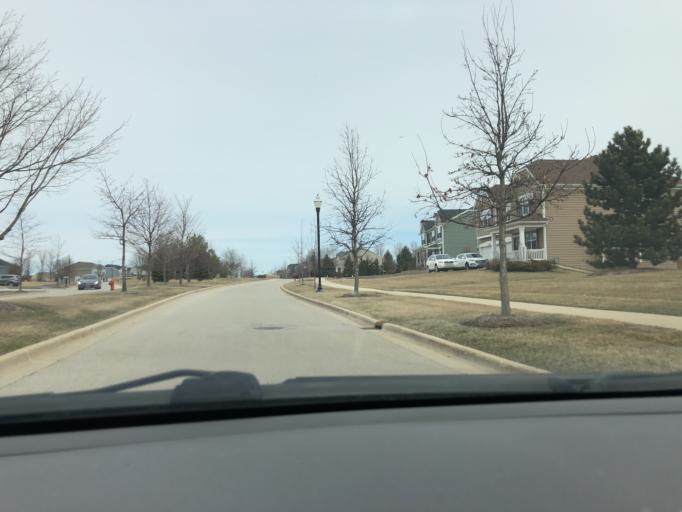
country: US
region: Illinois
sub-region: Kane County
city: Pingree Grove
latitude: 42.0307
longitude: -88.3569
